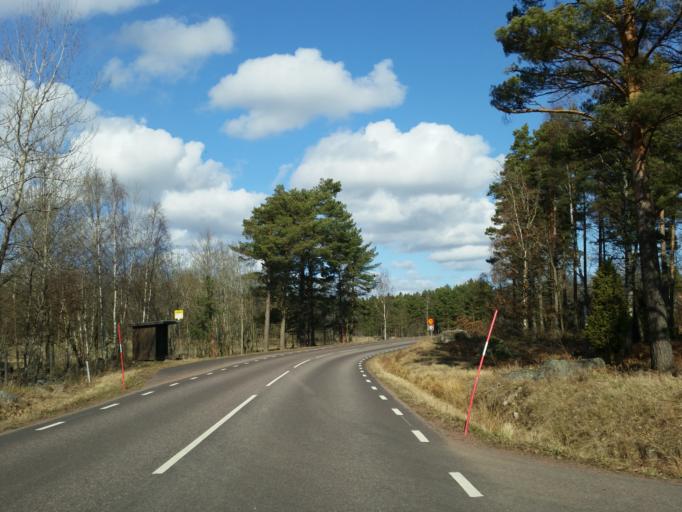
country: SE
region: Kalmar
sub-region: Monsteras Kommun
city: Timmernabben
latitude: 56.8775
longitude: 16.4313
